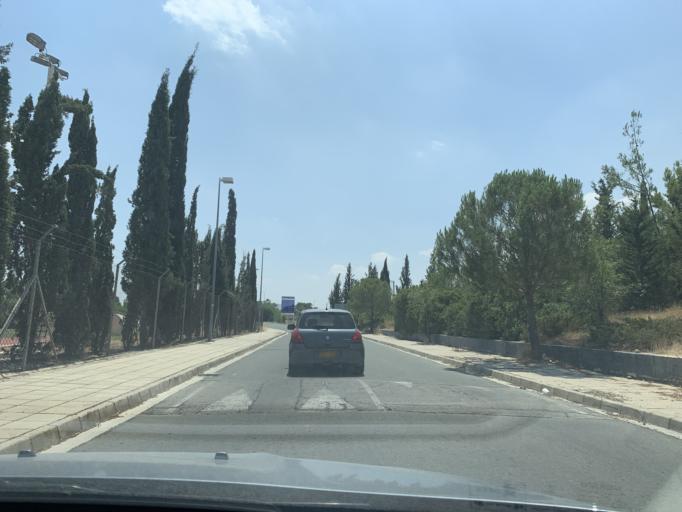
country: CY
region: Lefkosia
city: Tseri
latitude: 35.1145
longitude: 33.3591
